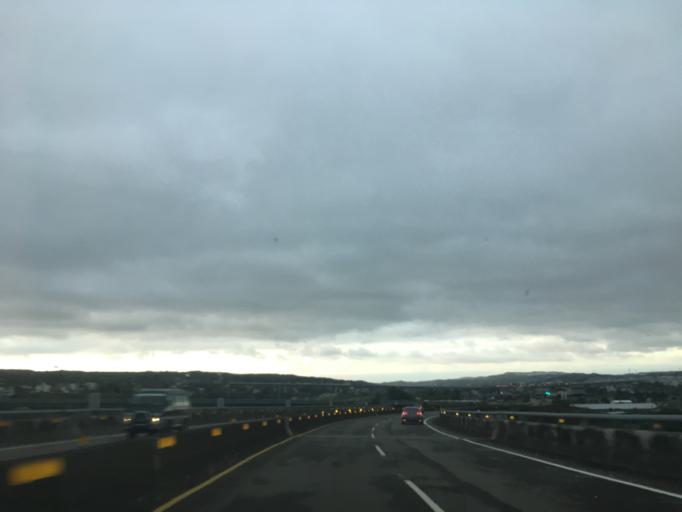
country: TW
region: Taiwan
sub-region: Miaoli
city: Miaoli
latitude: 24.4606
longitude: 120.7810
